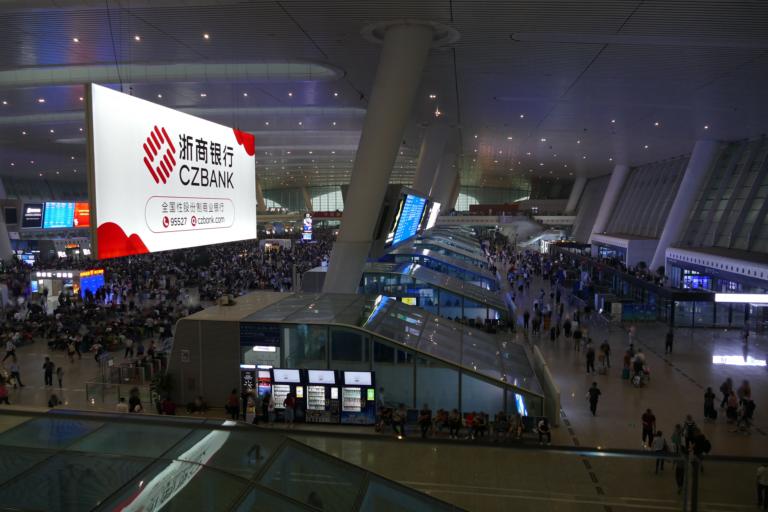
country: CN
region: Zhejiang Sheng
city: Pengbu
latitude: 30.2938
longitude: 120.2090
